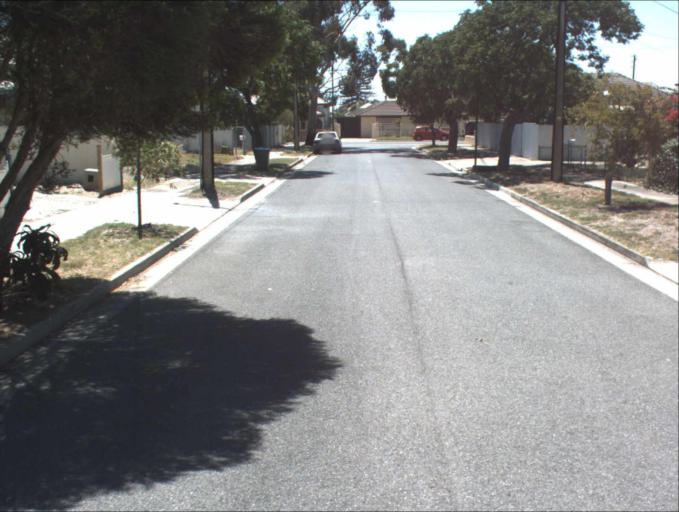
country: AU
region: South Australia
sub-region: Port Adelaide Enfield
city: Birkenhead
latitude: -34.8364
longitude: 138.4987
